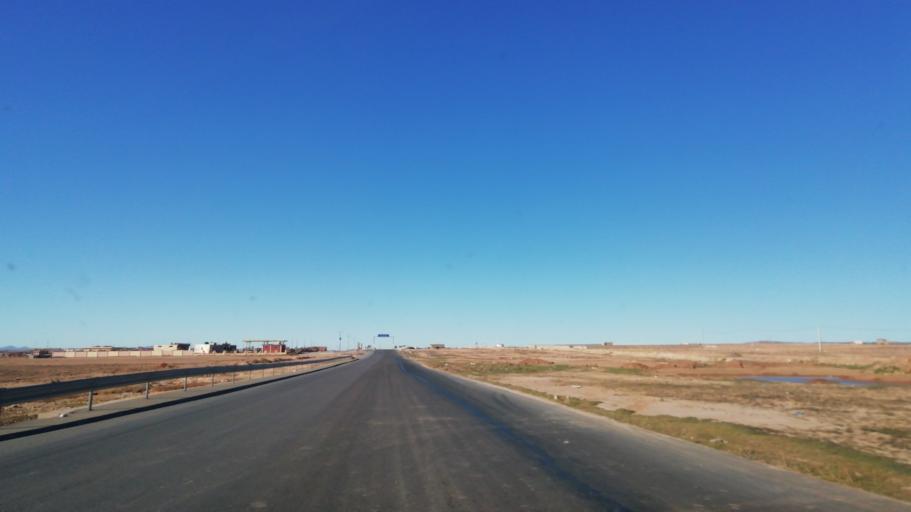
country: DZ
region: Tlemcen
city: Sebdou
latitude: 34.2072
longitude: -1.2397
